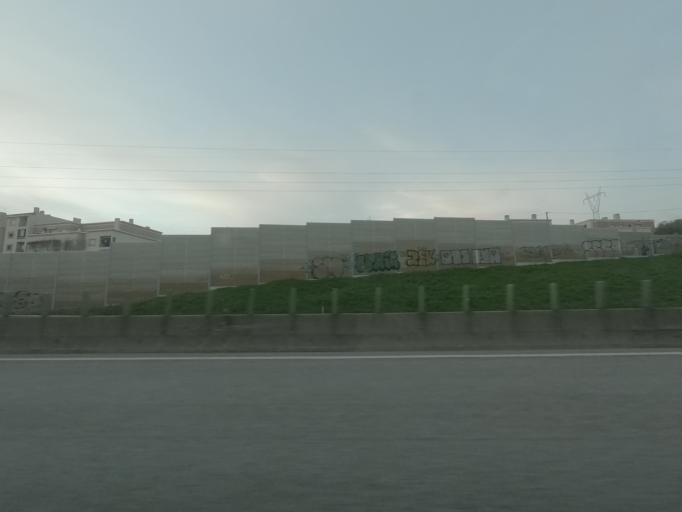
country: PT
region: Lisbon
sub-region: Vila Franca de Xira
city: Sobralinho
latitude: 38.9042
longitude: -9.0413
